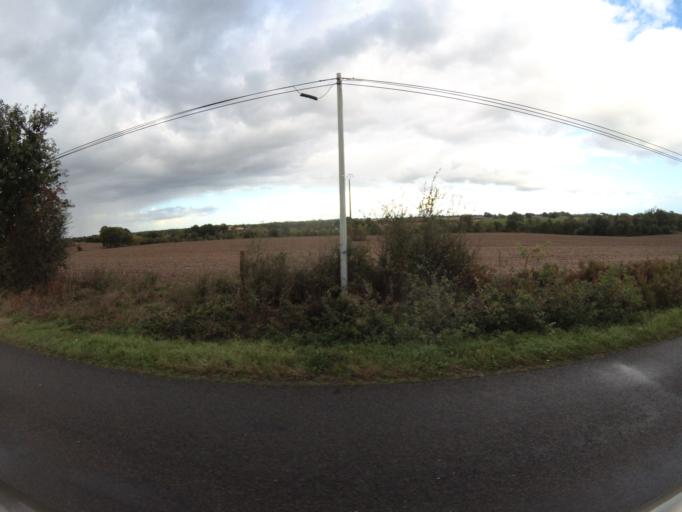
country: FR
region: Pays de la Loire
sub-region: Departement de la Loire-Atlantique
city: Saint-Hilaire-de-Clisson
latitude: 47.0691
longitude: -1.3229
